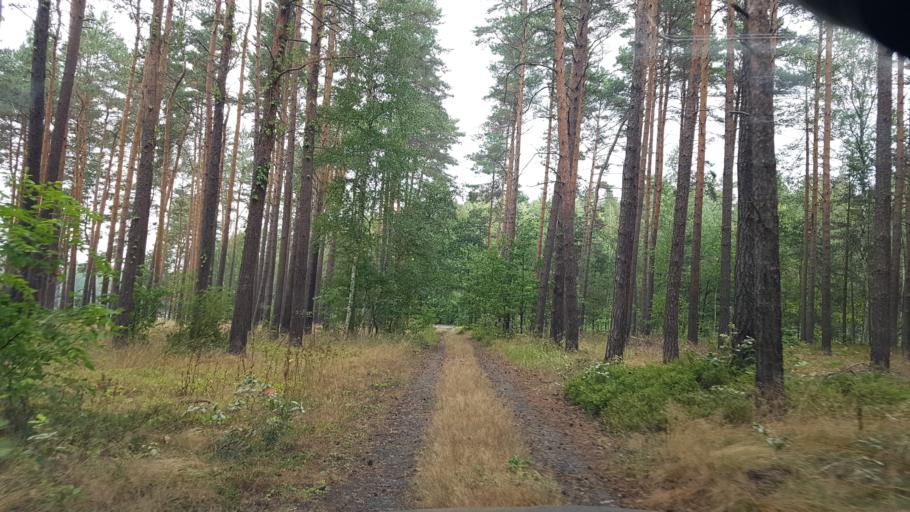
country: DE
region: Saxony
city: Bernsdorf
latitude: 51.3701
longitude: 14.0923
